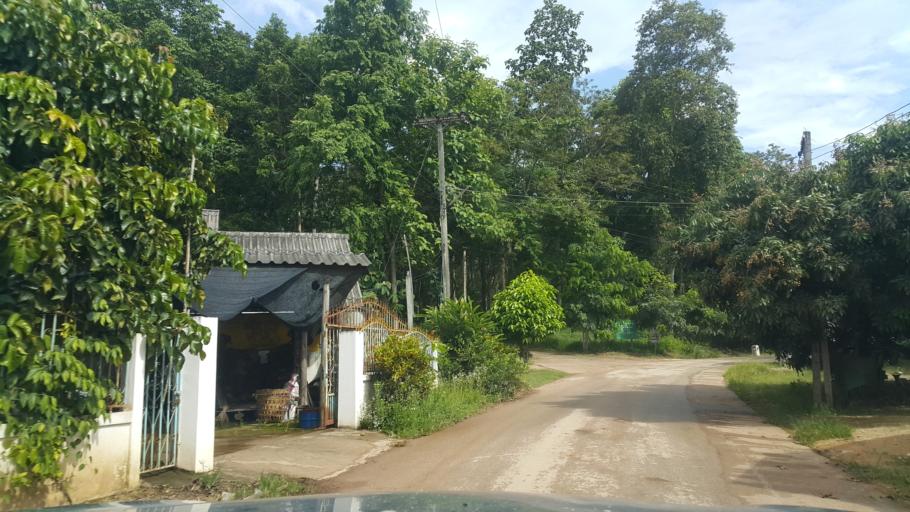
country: TH
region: Chiang Mai
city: Mae Taeng
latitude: 19.2108
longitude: 99.0073
